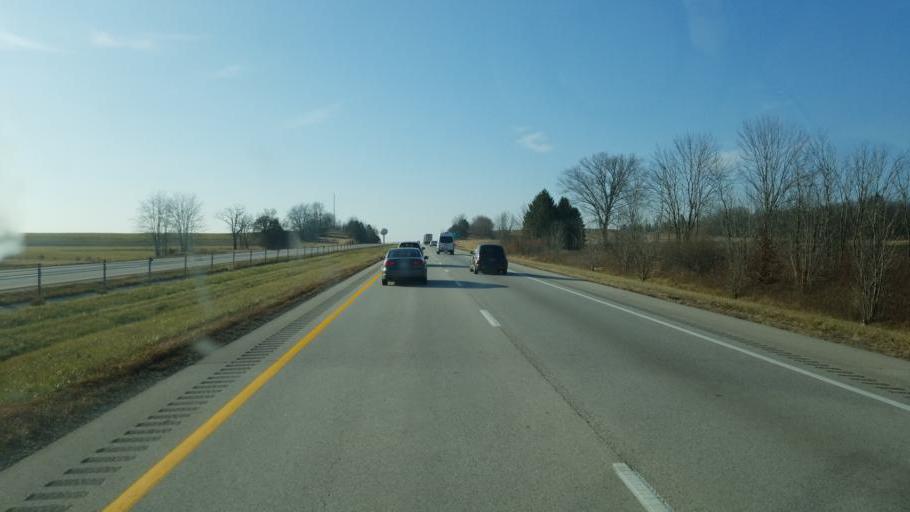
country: US
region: Ohio
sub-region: Medina County
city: Seville
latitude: 41.0331
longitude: -81.8544
